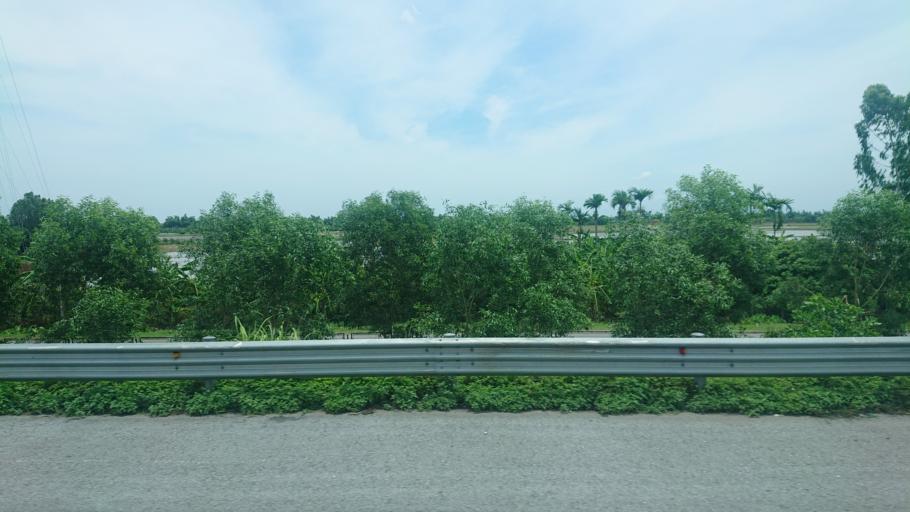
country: VN
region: Hai Duong
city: Tu Ky
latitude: 20.8367
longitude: 106.4307
